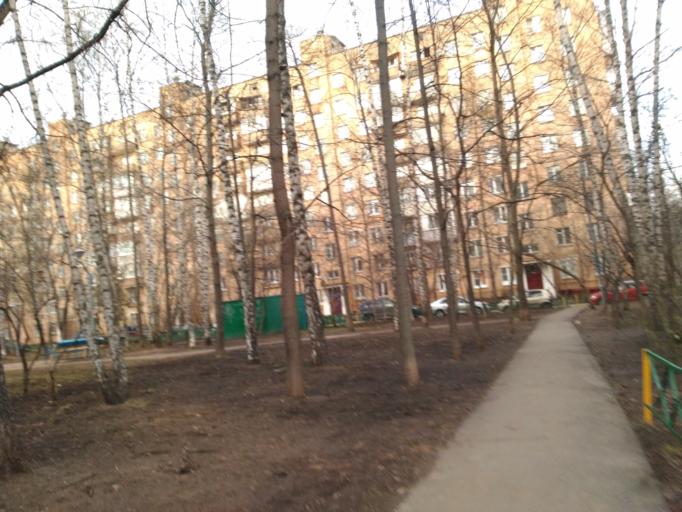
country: RU
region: Moskovskaya
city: Khoroshevo-Mnevniki
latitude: 55.7875
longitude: 37.4601
